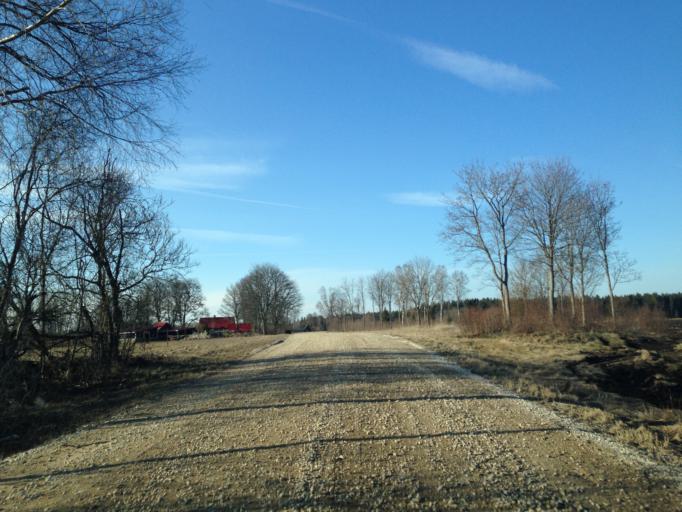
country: EE
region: Harju
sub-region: Nissi vald
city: Turba
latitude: 59.1603
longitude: 24.1437
